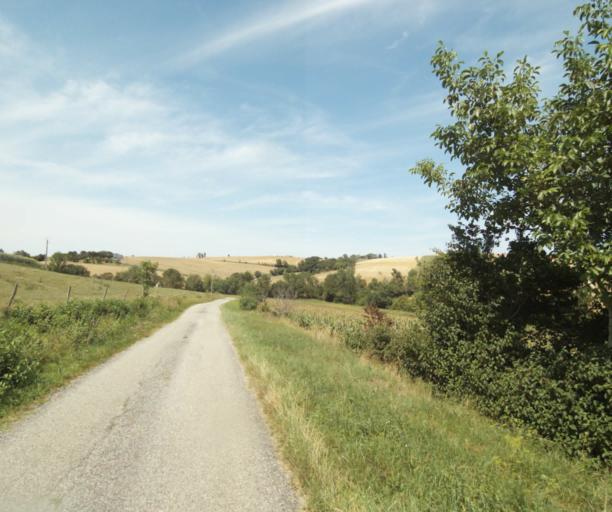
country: FR
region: Midi-Pyrenees
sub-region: Departement de l'Ariege
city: Lezat-sur-Leze
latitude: 43.2563
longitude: 1.4045
